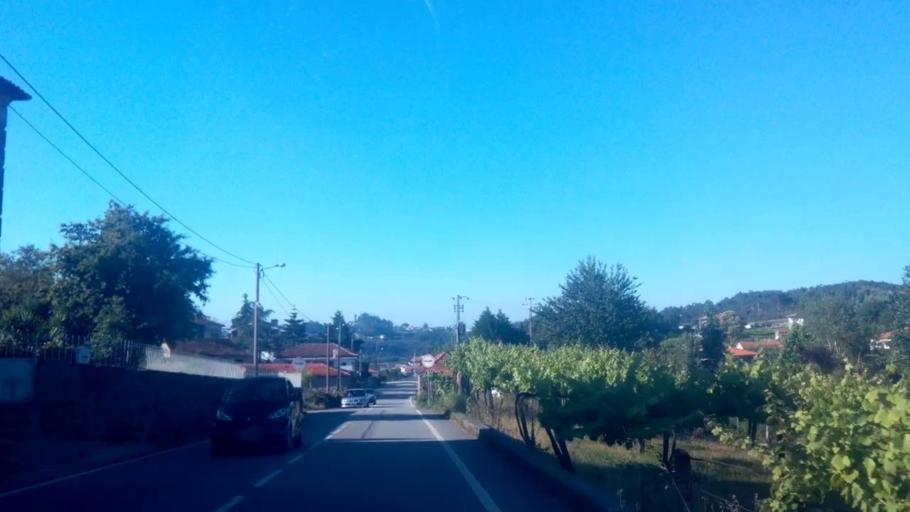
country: PT
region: Porto
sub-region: Penafiel
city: Penafiel
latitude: 41.1902
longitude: -8.2742
